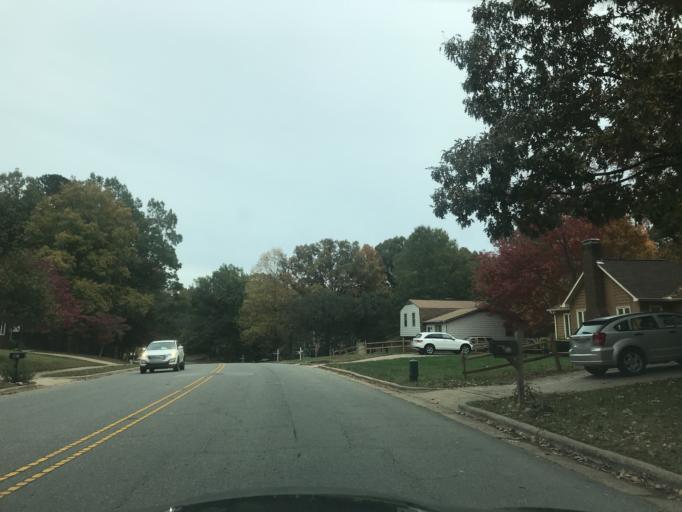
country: US
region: North Carolina
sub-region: Wake County
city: West Raleigh
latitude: 35.8826
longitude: -78.6575
